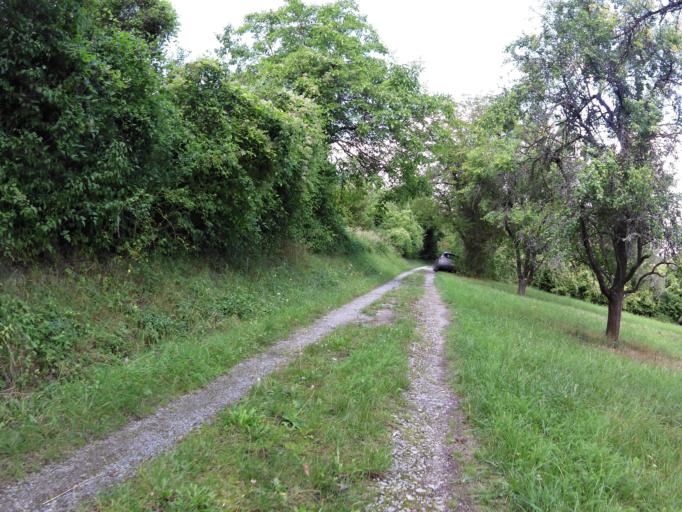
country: DE
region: Bavaria
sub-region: Regierungsbezirk Unterfranken
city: Margetshochheim
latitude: 49.8368
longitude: 9.8531
